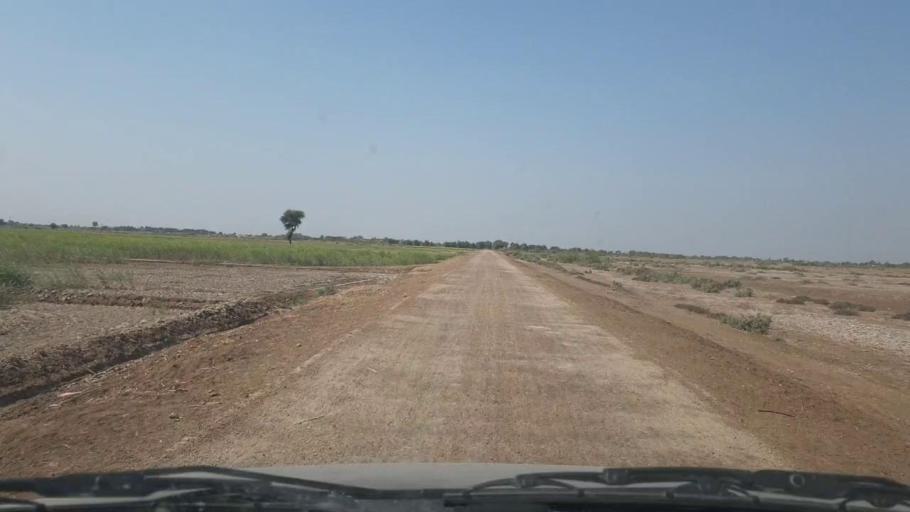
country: PK
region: Sindh
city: Samaro
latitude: 25.2341
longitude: 69.3353
